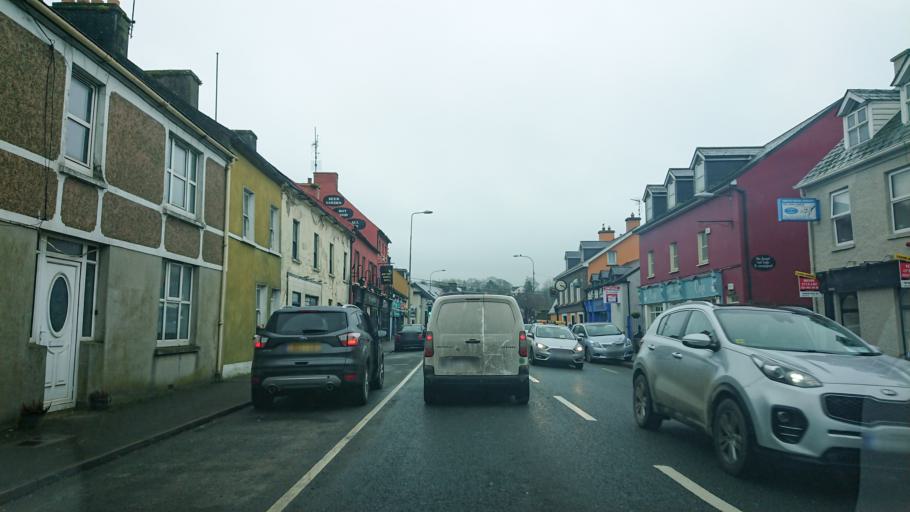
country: IE
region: Munster
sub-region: County Cork
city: Bandon
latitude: 51.7651
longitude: -8.6586
